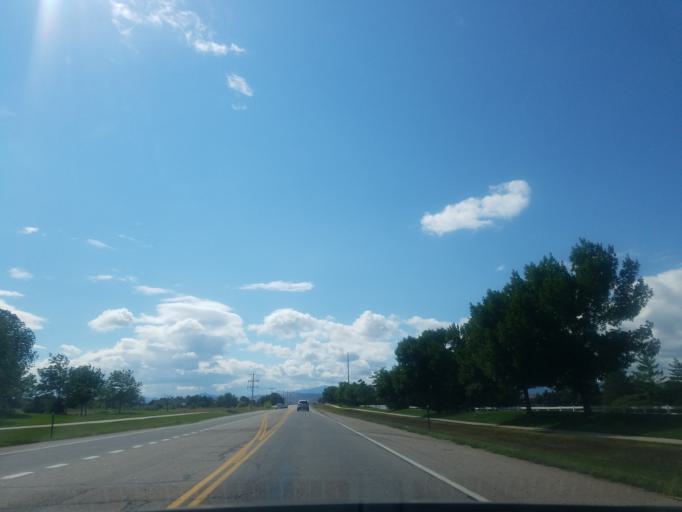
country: US
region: Colorado
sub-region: Larimer County
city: Loveland
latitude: 40.4802
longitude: -105.0457
